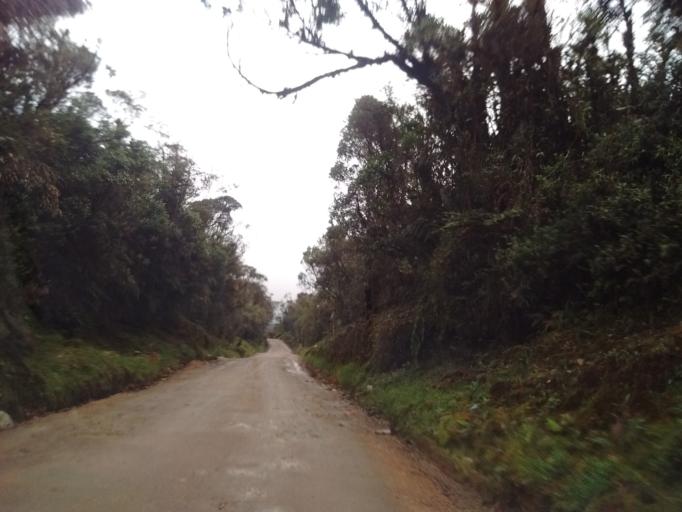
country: CO
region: Huila
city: Isnos
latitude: 2.1203
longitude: -76.3764
